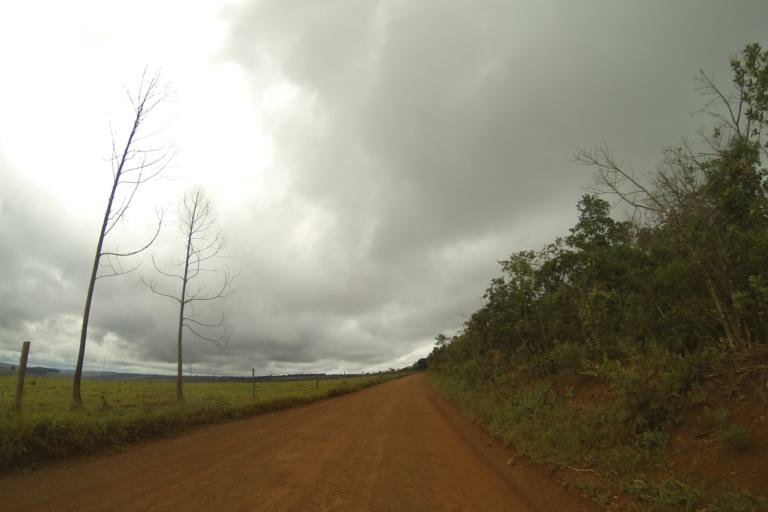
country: BR
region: Minas Gerais
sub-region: Campos Altos
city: Campos Altos
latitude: -19.8377
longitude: -46.3238
